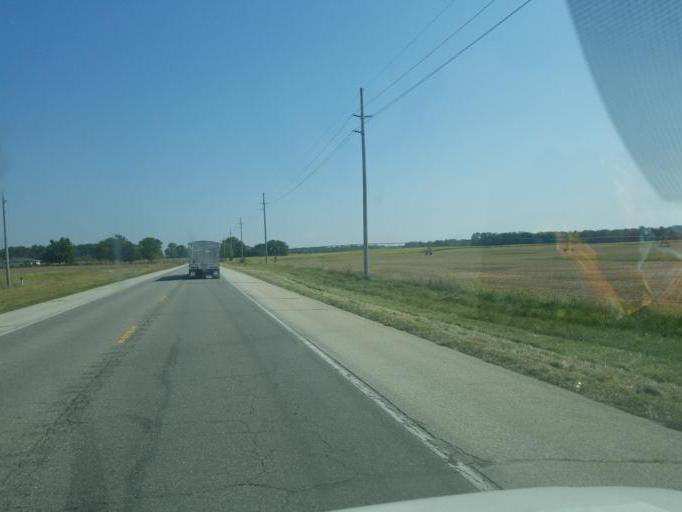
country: US
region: Indiana
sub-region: LaGrange County
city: Lagrange
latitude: 41.6419
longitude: -85.2392
